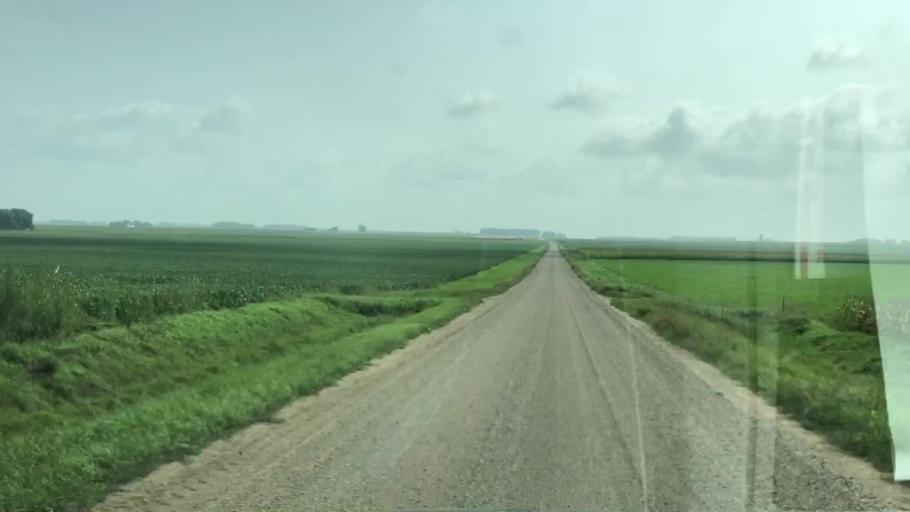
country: US
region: Iowa
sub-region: O'Brien County
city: Sheldon
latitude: 43.2152
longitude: -95.9334
